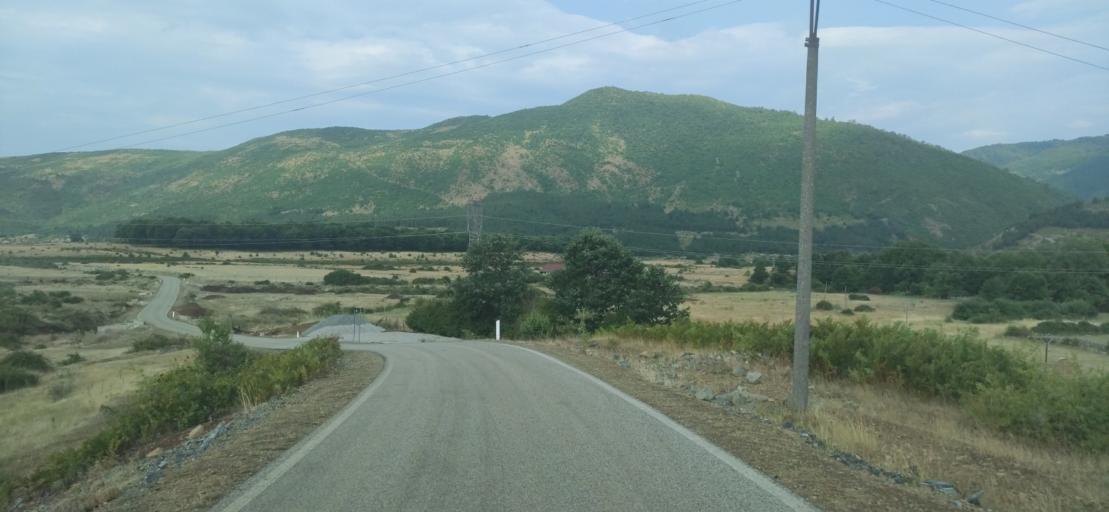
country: AL
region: Shkoder
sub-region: Rrethi i Pukes
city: Iballe
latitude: 42.1869
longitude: 19.9971
